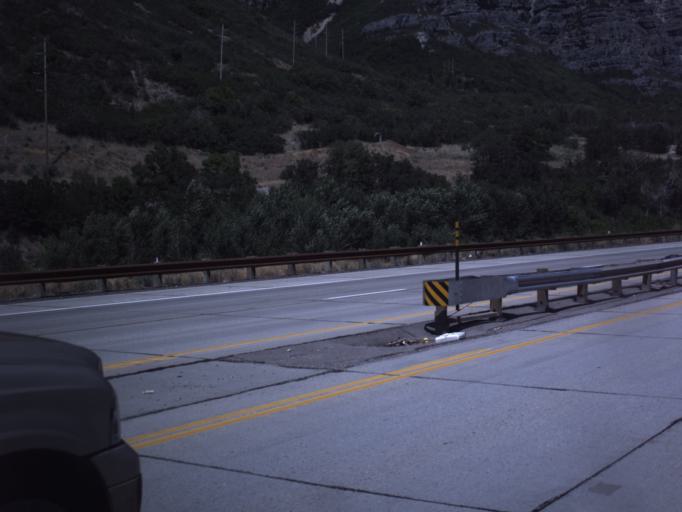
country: US
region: Utah
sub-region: Utah County
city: Orem
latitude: 40.3389
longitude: -111.6092
